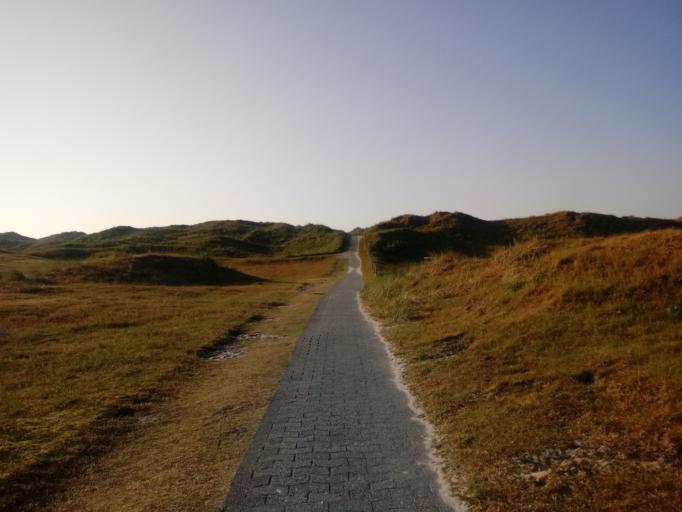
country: DE
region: Lower Saxony
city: Baltrum
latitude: 53.7323
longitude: 7.3969
